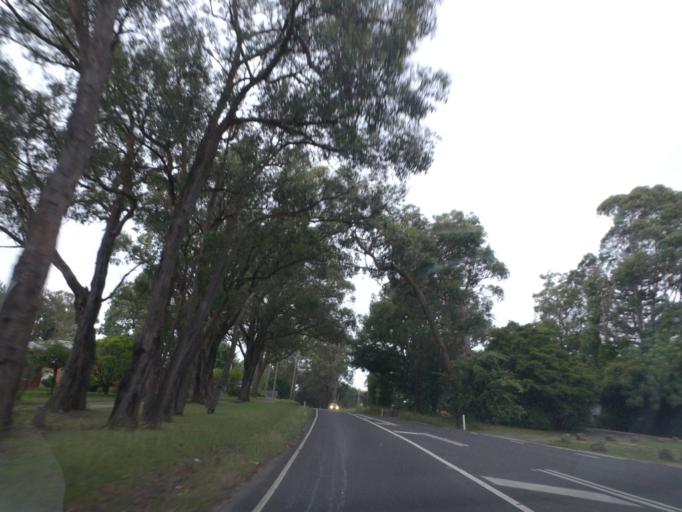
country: AU
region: Victoria
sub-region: Yarra Ranges
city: Mount Evelyn
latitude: -37.7894
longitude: 145.3958
